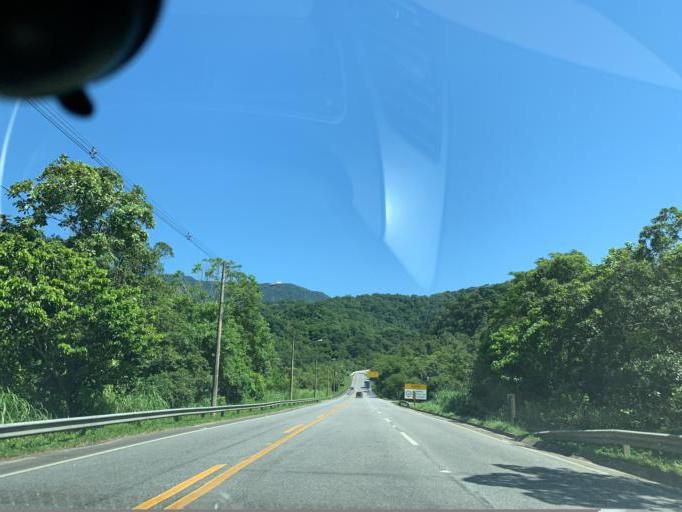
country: BR
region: Sao Paulo
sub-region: Bertioga
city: Bertioga
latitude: -23.7586
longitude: -46.0387
